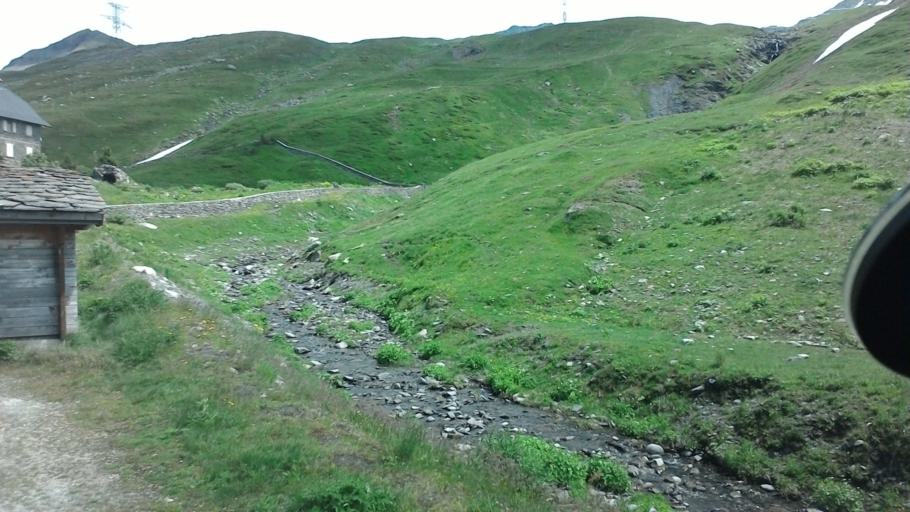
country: IT
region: Aosta Valley
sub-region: Valle d'Aosta
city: La Thuile
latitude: 45.6742
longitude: 6.8790
